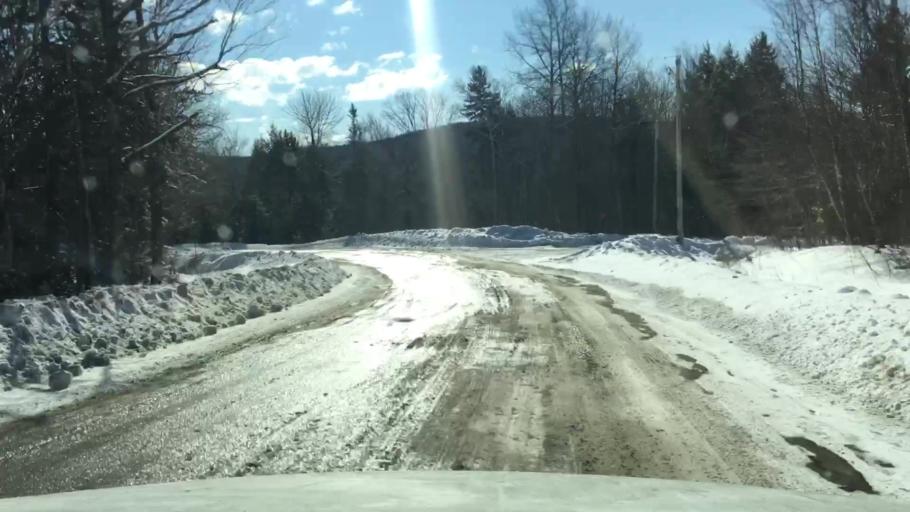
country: US
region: Maine
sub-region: Washington County
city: Calais
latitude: 45.0714
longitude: -67.4995
